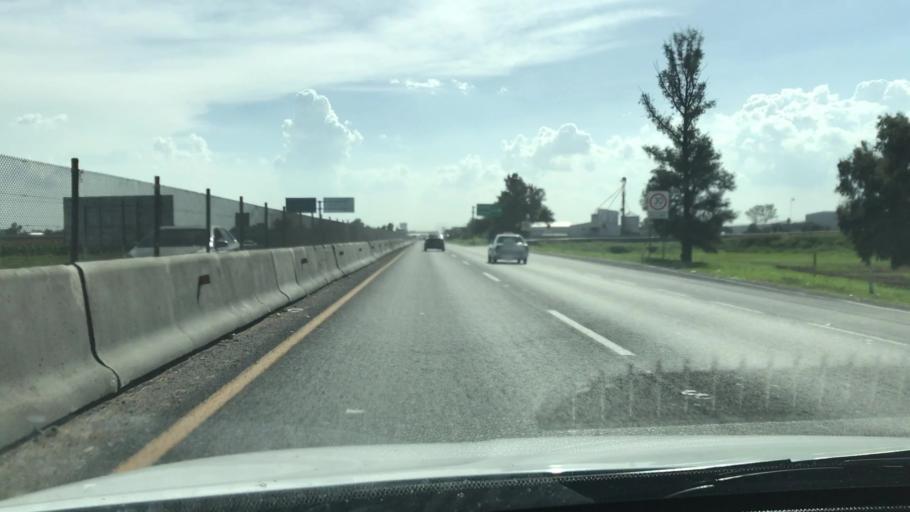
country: MX
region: Guanajuato
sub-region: Celaya
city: Colonia Pedro Maria Anaya
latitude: 20.5170
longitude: -100.8727
